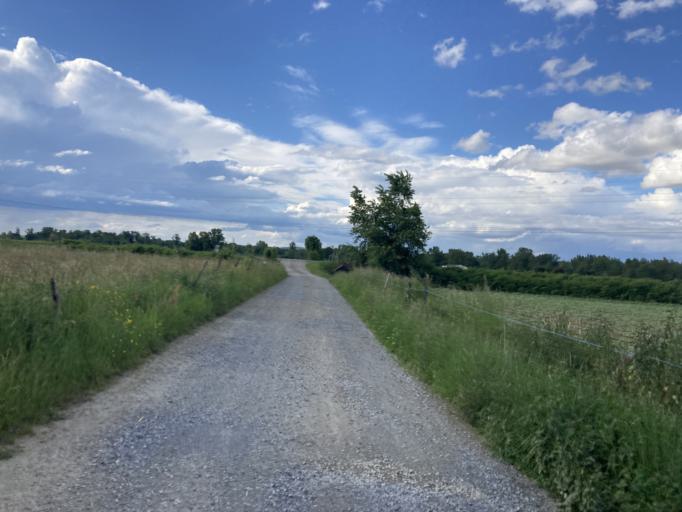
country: FR
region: Aquitaine
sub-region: Departement des Pyrenees-Atlantiques
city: Arbus
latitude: 43.3373
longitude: -0.5053
